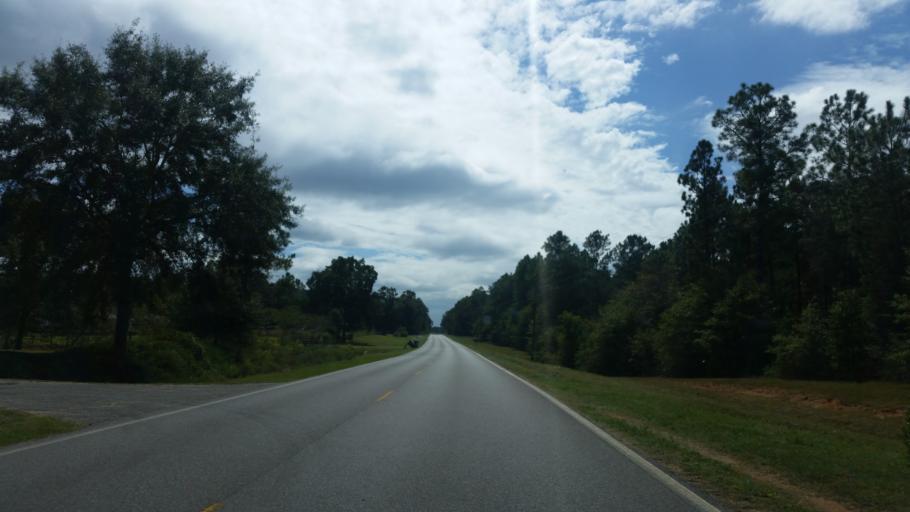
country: US
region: Florida
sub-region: Santa Rosa County
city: Point Baker
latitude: 30.7632
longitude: -86.9426
